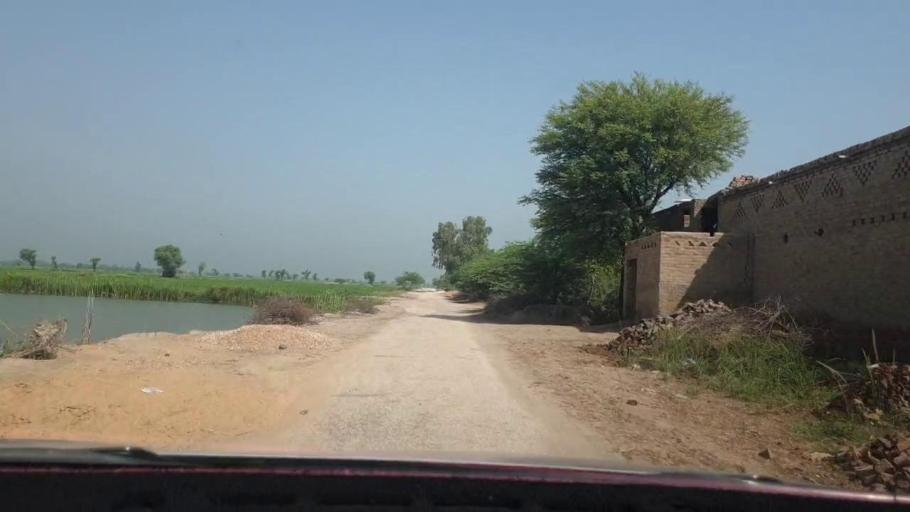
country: PK
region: Sindh
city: Nasirabad
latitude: 27.4256
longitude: 67.9044
